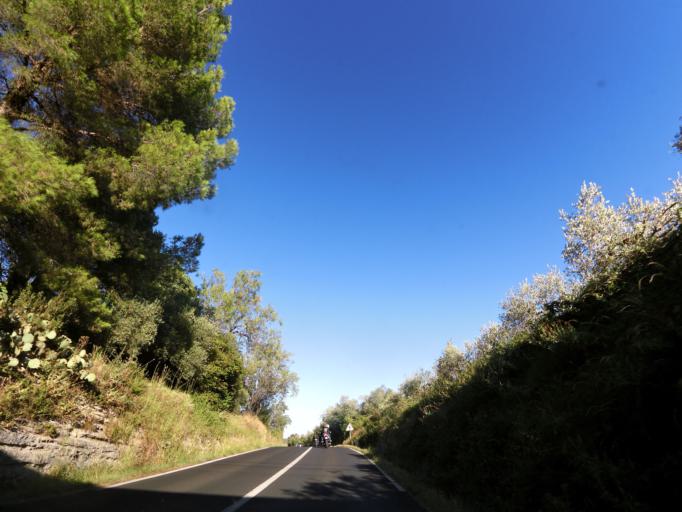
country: FR
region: Languedoc-Roussillon
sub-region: Departement du Gard
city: Villevieille
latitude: 43.7923
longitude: 4.0995
